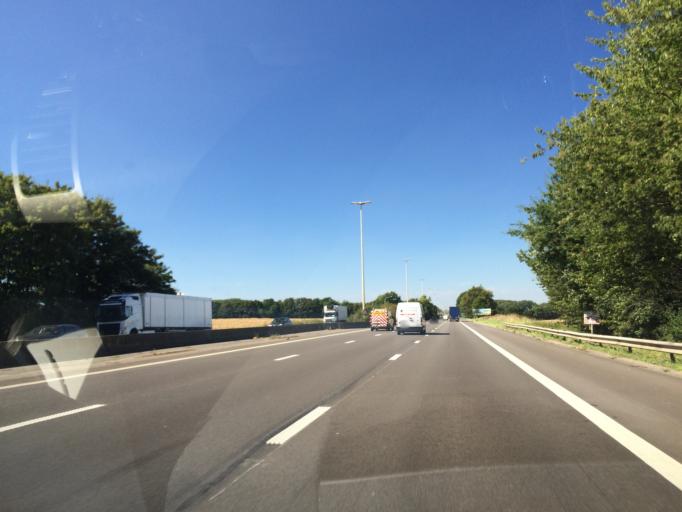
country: BE
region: Wallonia
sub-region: Province du Brabant Wallon
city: Perwez
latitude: 50.6147
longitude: 4.7725
